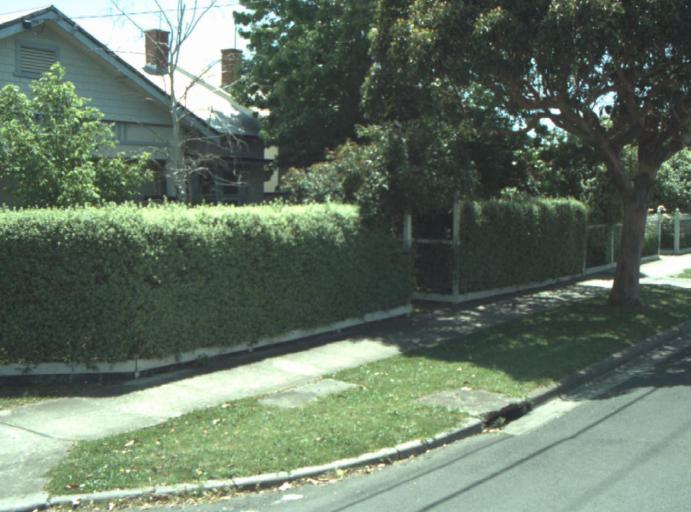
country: AU
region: Victoria
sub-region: Greater Geelong
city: Geelong West
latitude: -38.1397
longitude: 144.3300
